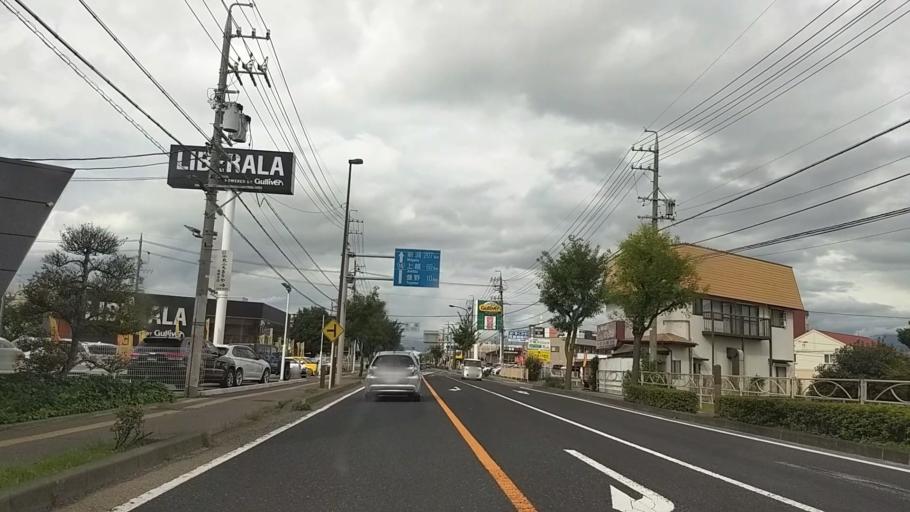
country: JP
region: Nagano
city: Nagano-shi
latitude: 36.6480
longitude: 138.2204
